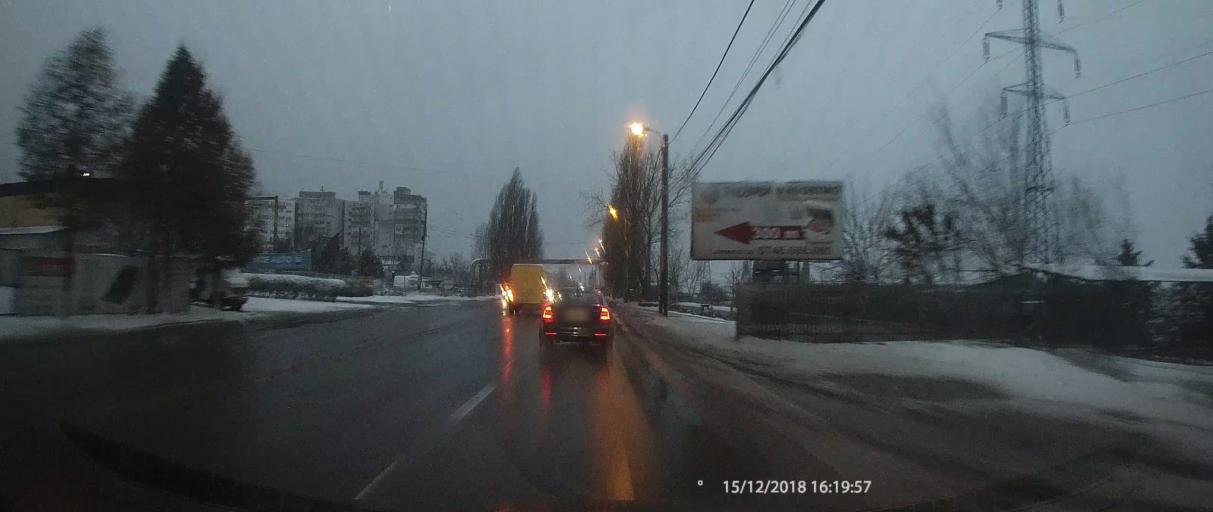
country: RO
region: Galati
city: Galati
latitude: 45.4164
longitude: 28.0048
